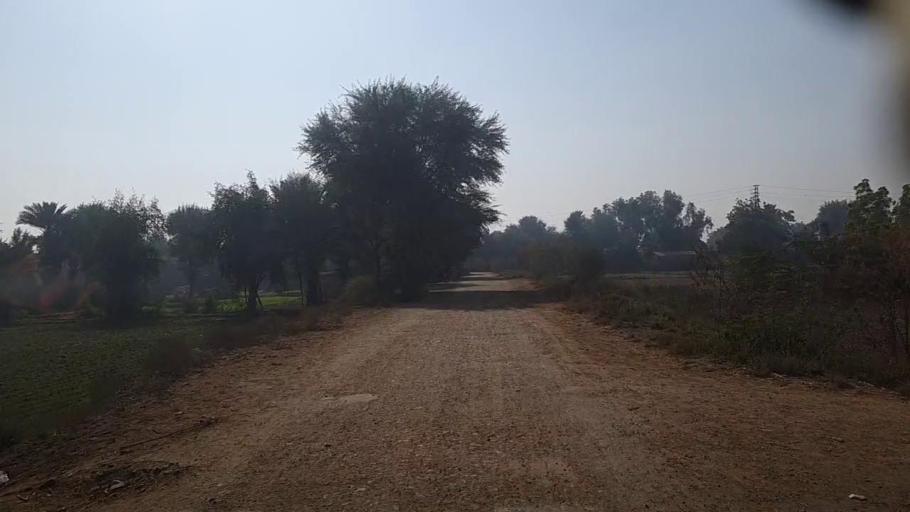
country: PK
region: Sindh
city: Kandiari
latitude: 27.0259
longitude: 68.5058
